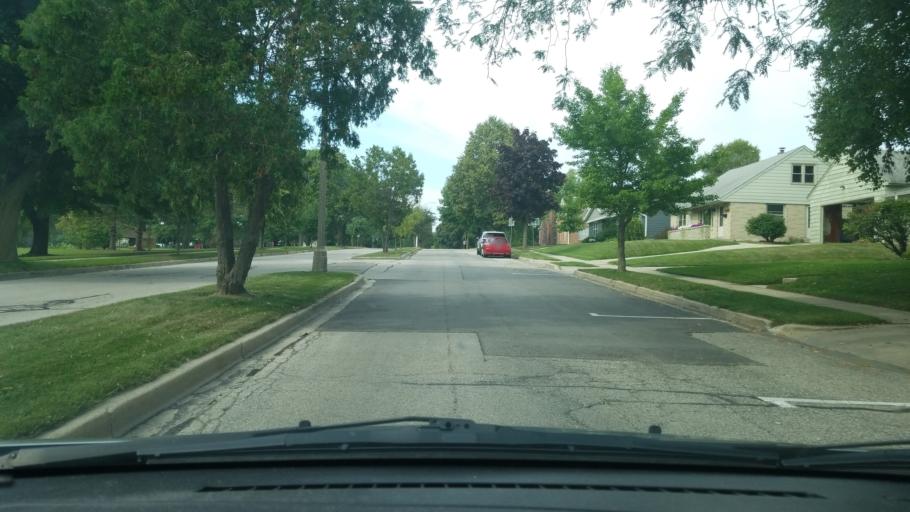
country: US
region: Wisconsin
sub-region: Ozaukee County
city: Cedarburg
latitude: 43.3041
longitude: -87.9945
